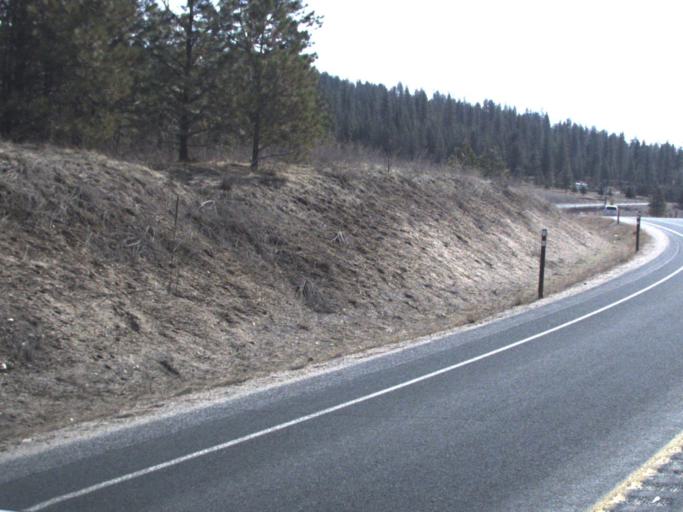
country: US
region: Washington
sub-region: Stevens County
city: Colville
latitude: 48.5107
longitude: -117.7288
